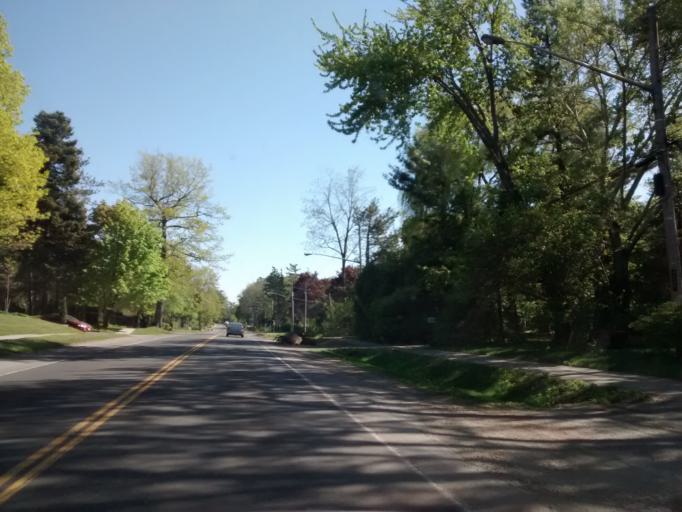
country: CA
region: Ontario
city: Oakville
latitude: 43.4160
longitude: -79.6911
